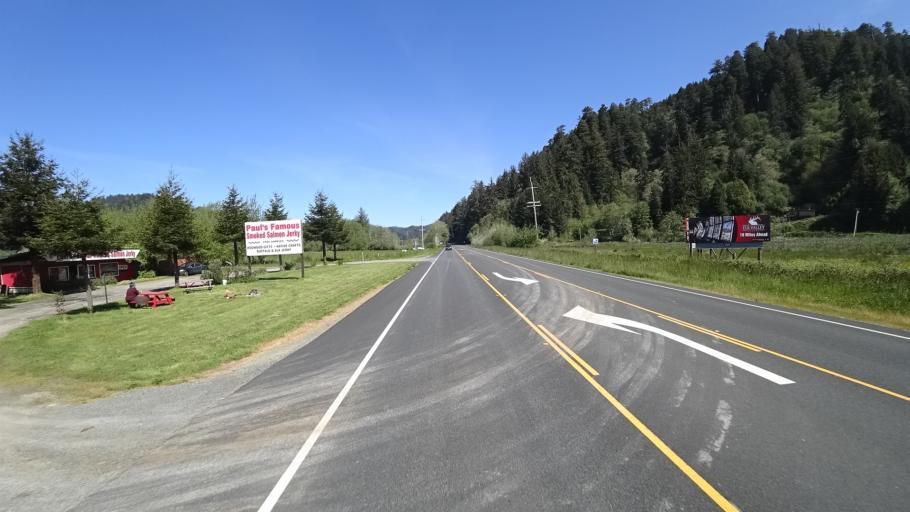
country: US
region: California
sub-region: Del Norte County
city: Bertsch-Oceanview
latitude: 41.5438
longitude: -124.0512
